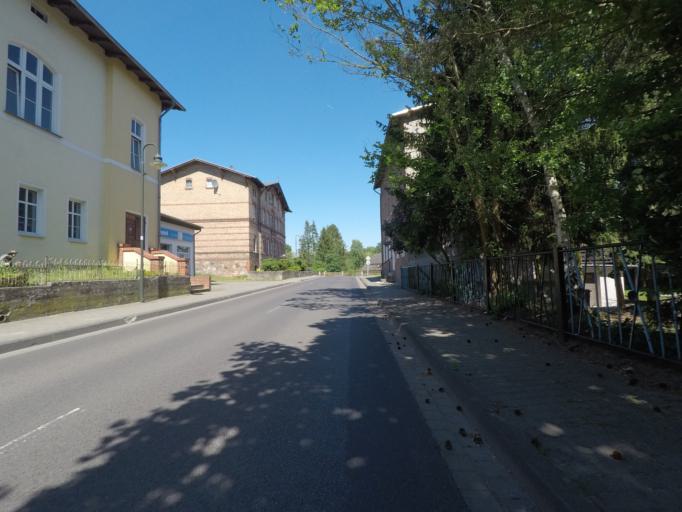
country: DE
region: Brandenburg
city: Eberswalde
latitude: 52.8104
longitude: 13.7760
